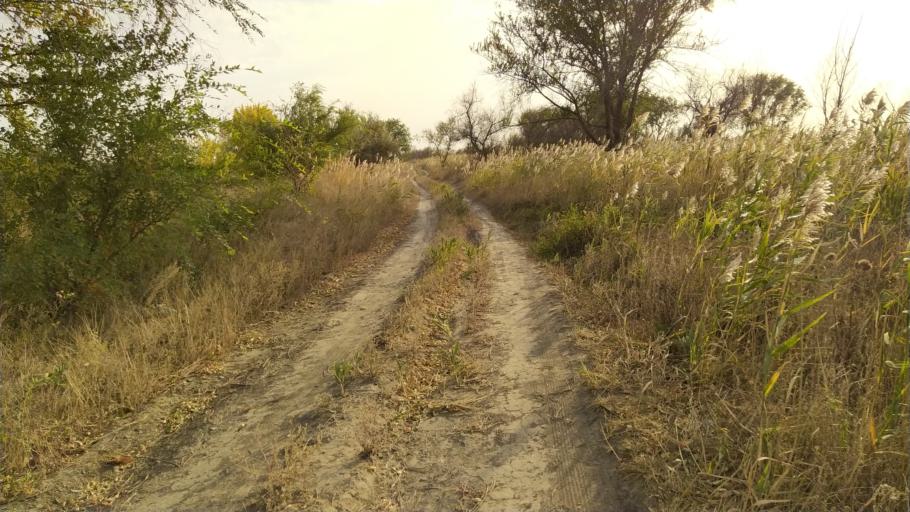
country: RU
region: Rostov
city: Kuleshovka
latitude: 47.1220
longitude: 39.6029
